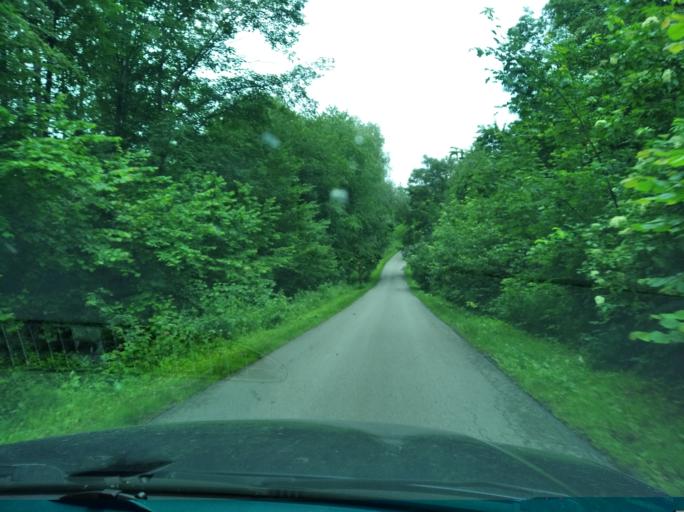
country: PL
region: Subcarpathian Voivodeship
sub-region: Powiat jaroslawski
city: Pruchnik
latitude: 49.8946
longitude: 22.5217
